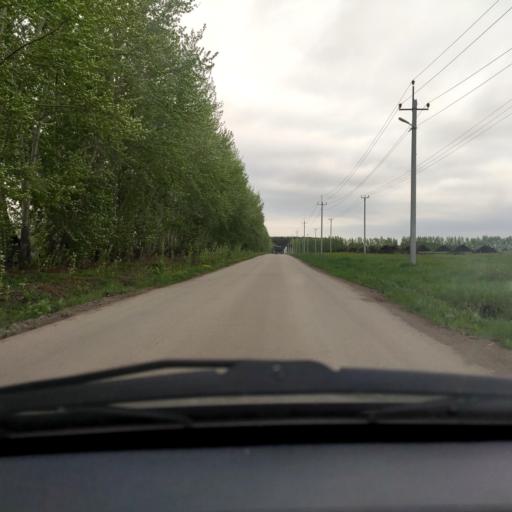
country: RU
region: Bashkortostan
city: Kabakovo
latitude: 54.6193
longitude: 56.1596
